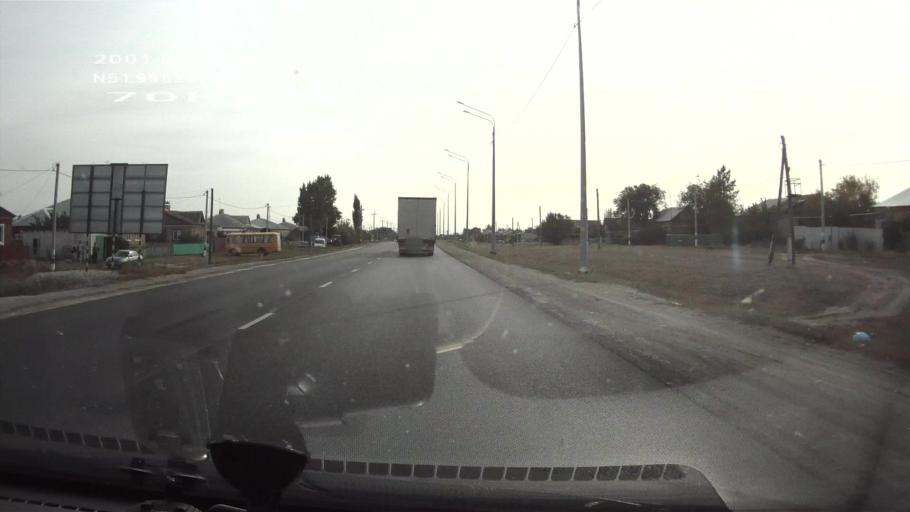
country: RU
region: Saratov
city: Sinodskoye
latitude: 51.9949
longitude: 46.6725
